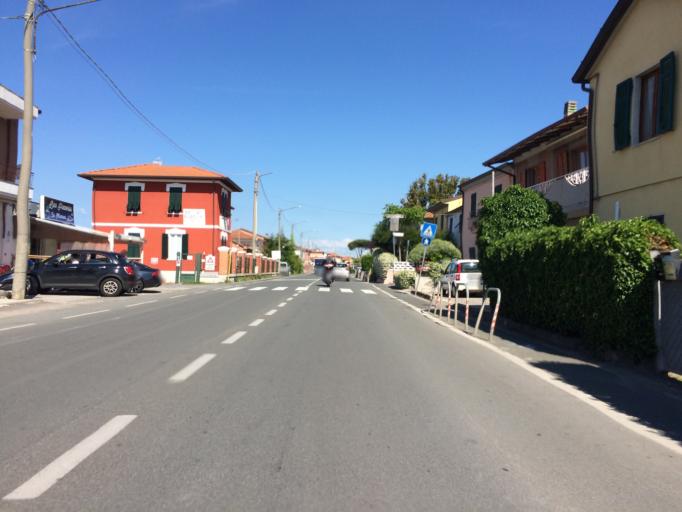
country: IT
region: Liguria
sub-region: Provincia di La Spezia
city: Casano-Dogana-Isola
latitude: 44.0674
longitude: 10.0293
